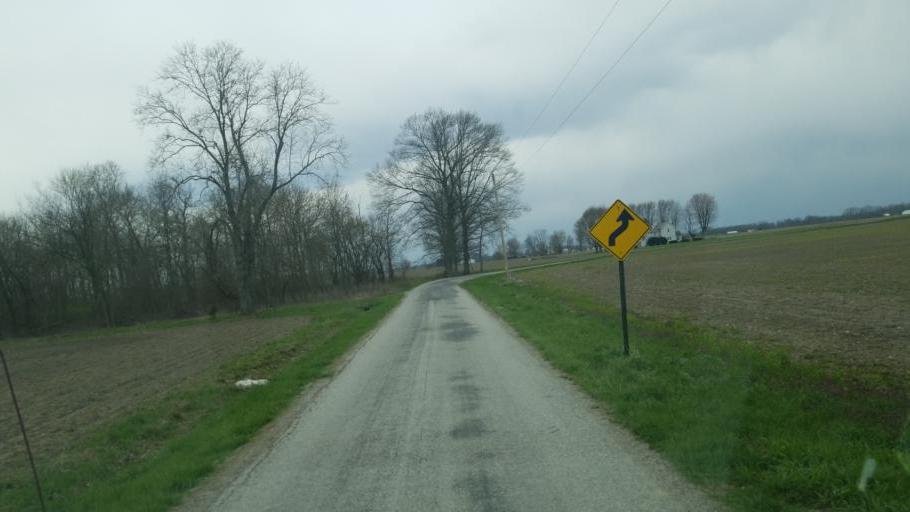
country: US
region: Ohio
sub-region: Union County
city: Richwood
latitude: 40.3839
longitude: -83.2329
